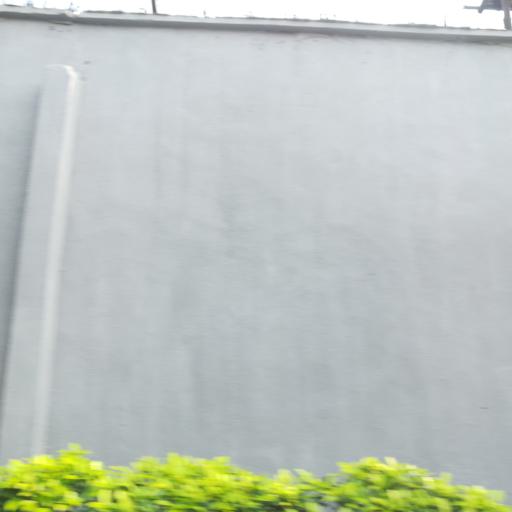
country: NG
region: Rivers
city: Port Harcourt
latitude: 4.8466
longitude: 7.0569
